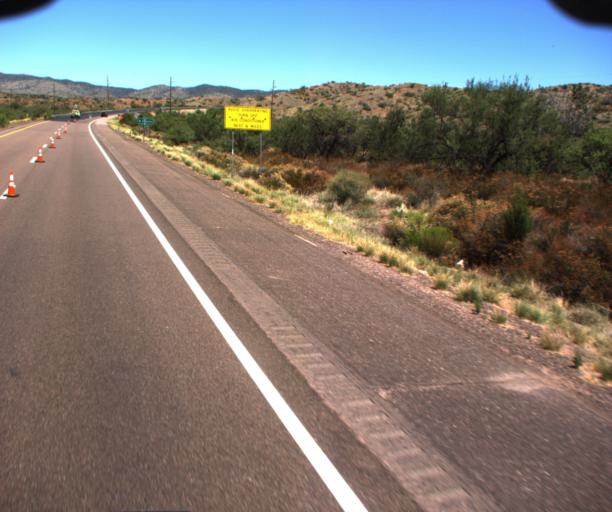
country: US
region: Arizona
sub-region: Gila County
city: Payson
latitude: 34.1092
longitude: -111.3535
